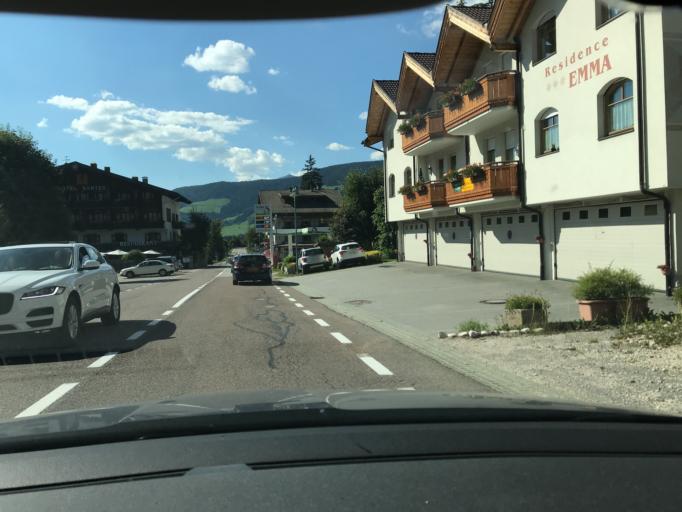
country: IT
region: Trentino-Alto Adige
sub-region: Bolzano
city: Dobbiaco
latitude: 46.7208
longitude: 12.2255
